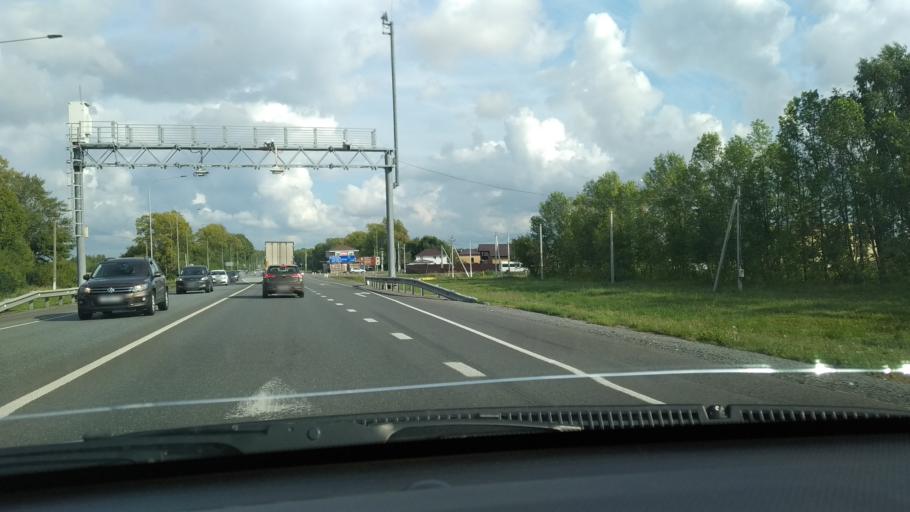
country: RU
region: Tatarstan
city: Stolbishchi
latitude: 55.6566
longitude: 49.3098
